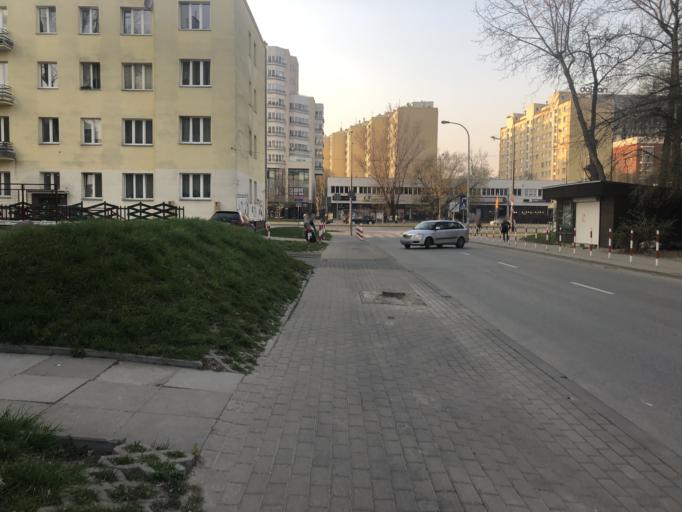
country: PL
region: Masovian Voivodeship
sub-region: Warszawa
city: Ochota
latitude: 52.2280
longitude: 20.9686
